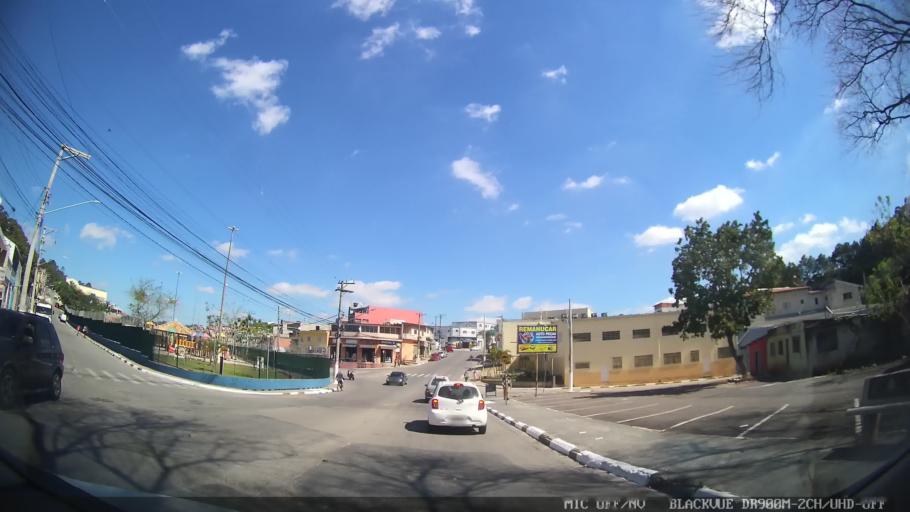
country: BR
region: Sao Paulo
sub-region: Cajamar
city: Cajamar
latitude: -23.4234
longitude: -46.8255
